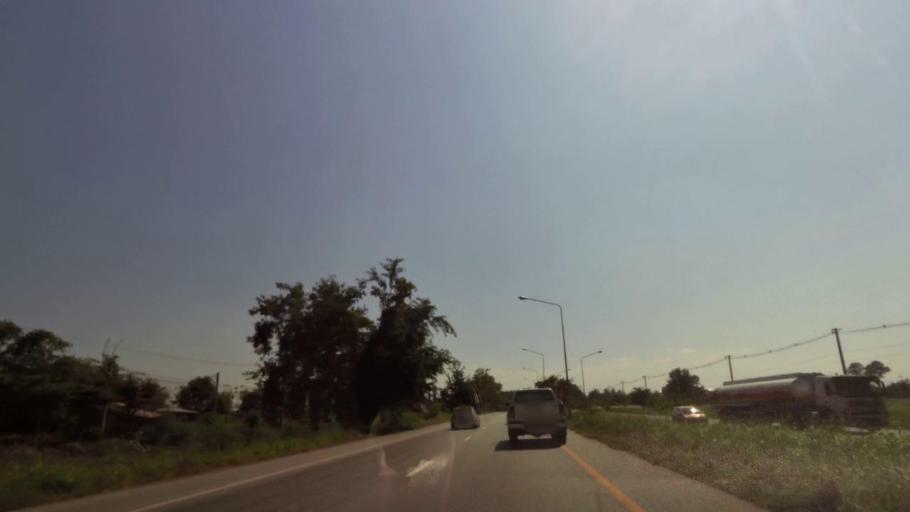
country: TH
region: Nakhon Sawan
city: Kao Liao
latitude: 15.8266
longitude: 100.1189
